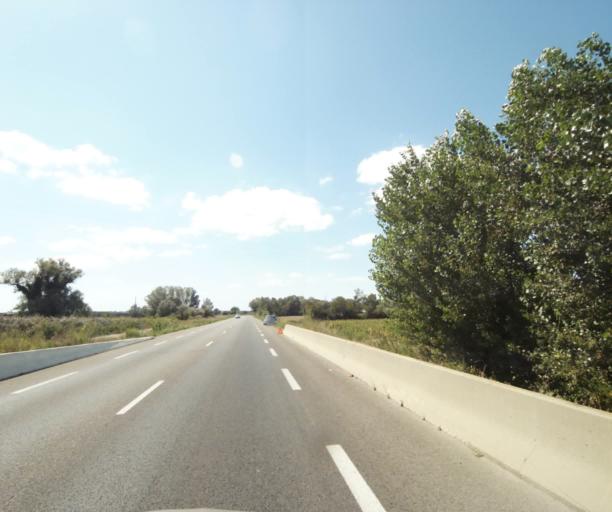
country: FR
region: Languedoc-Roussillon
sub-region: Departement du Gard
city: Rodilhan
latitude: 43.8209
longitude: 4.4177
